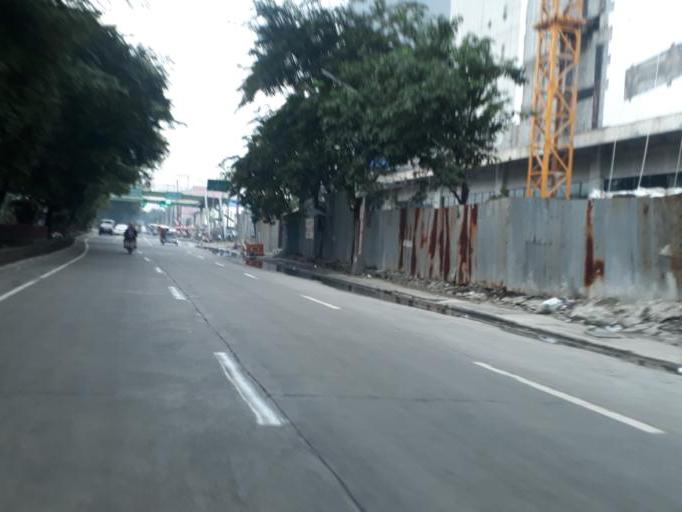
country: PH
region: Metro Manila
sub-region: Caloocan City
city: Niugan
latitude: 14.6570
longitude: 120.9606
